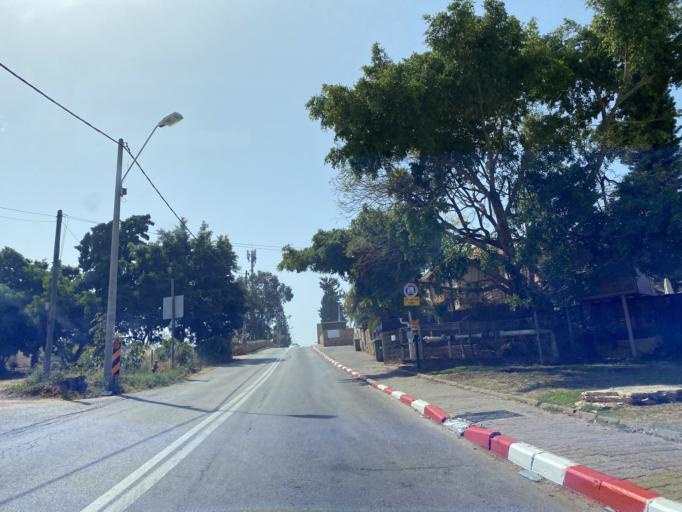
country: IL
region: Central District
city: Ra'anana
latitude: 32.1734
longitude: 34.8753
